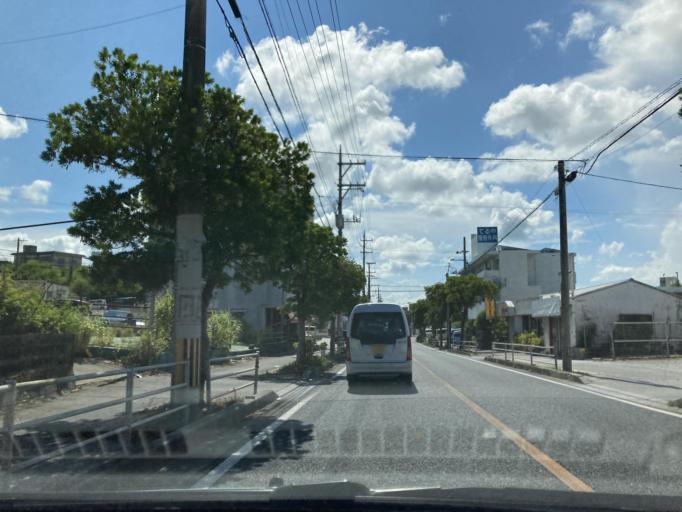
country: JP
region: Okinawa
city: Tomigusuku
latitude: 26.1846
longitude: 127.7122
